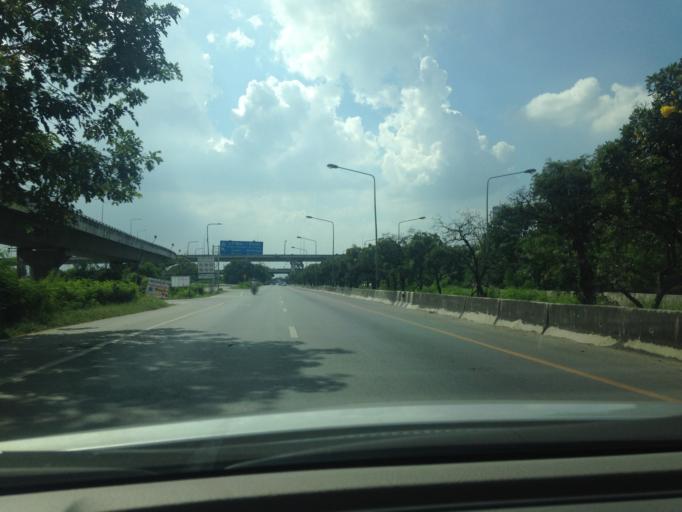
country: TH
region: Pathum Thani
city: Sam Khok
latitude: 14.0659
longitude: 100.5834
